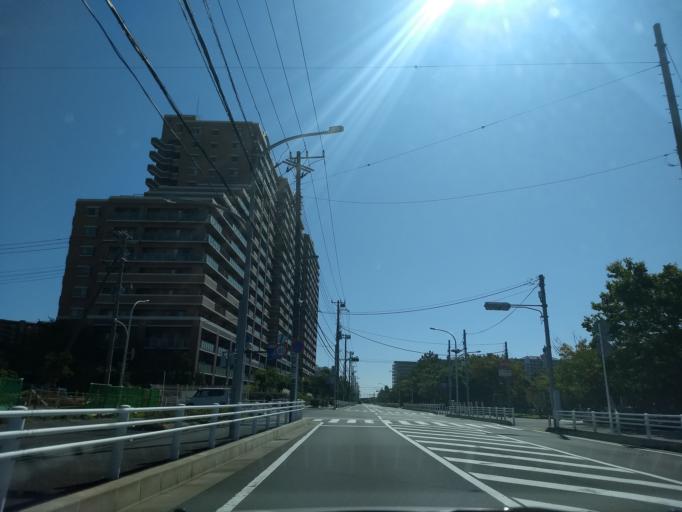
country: JP
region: Tokyo
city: Urayasu
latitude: 35.6380
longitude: 139.9150
